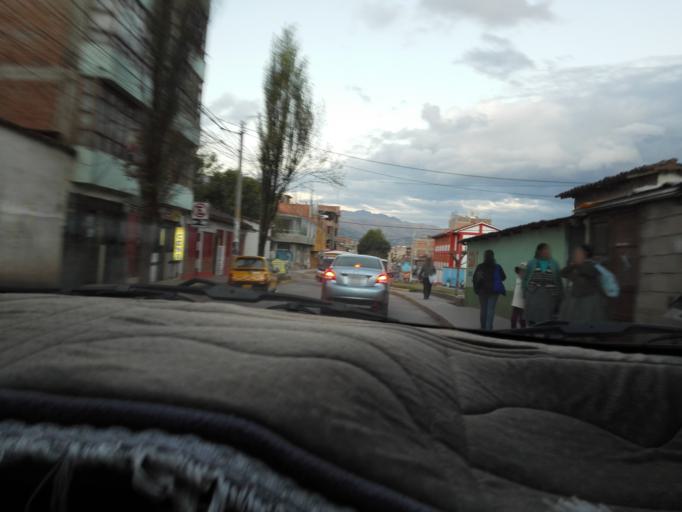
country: PE
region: Cusco
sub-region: Provincia de Cusco
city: Cusco
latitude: -13.5306
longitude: -71.9606
